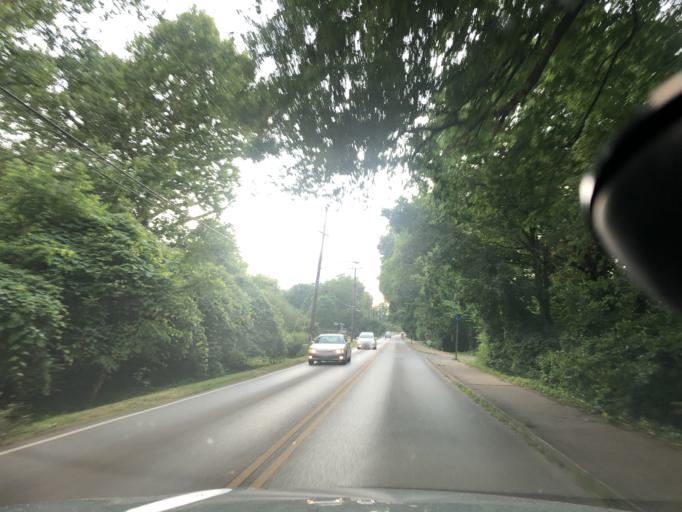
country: US
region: Tennessee
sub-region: Davidson County
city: Oak Hill
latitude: 36.1015
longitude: -86.8036
